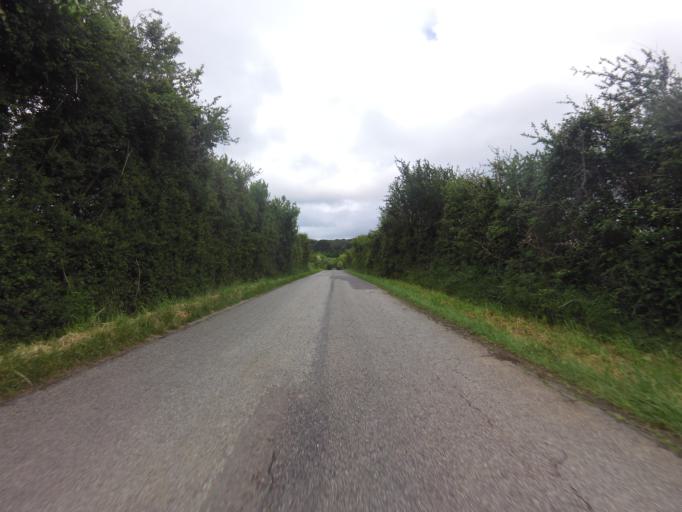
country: FR
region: Brittany
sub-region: Departement du Morbihan
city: Baden
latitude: 47.6084
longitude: -2.9323
